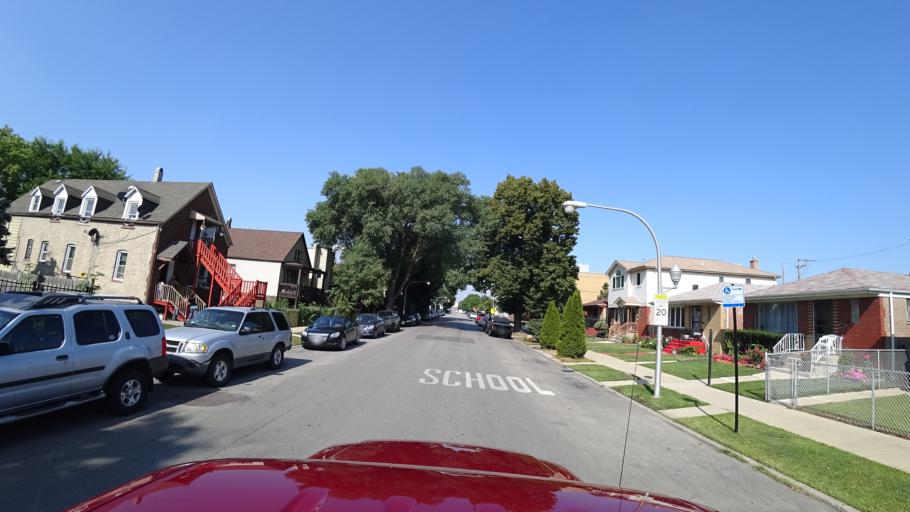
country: US
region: Illinois
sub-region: Cook County
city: Cicero
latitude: 41.8243
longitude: -87.7100
